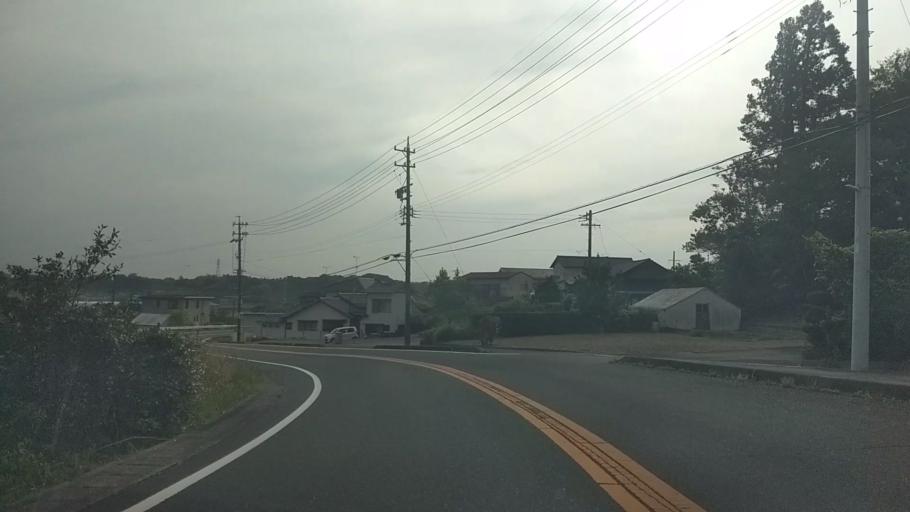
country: JP
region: Shizuoka
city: Kosai-shi
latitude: 34.7471
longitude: 137.6098
